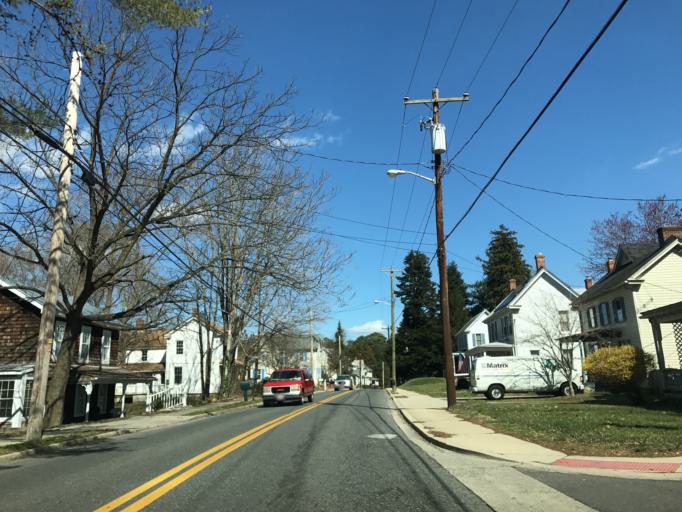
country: US
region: Maryland
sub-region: Queen Anne's County
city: Kingstown
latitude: 39.1434
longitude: -75.9843
